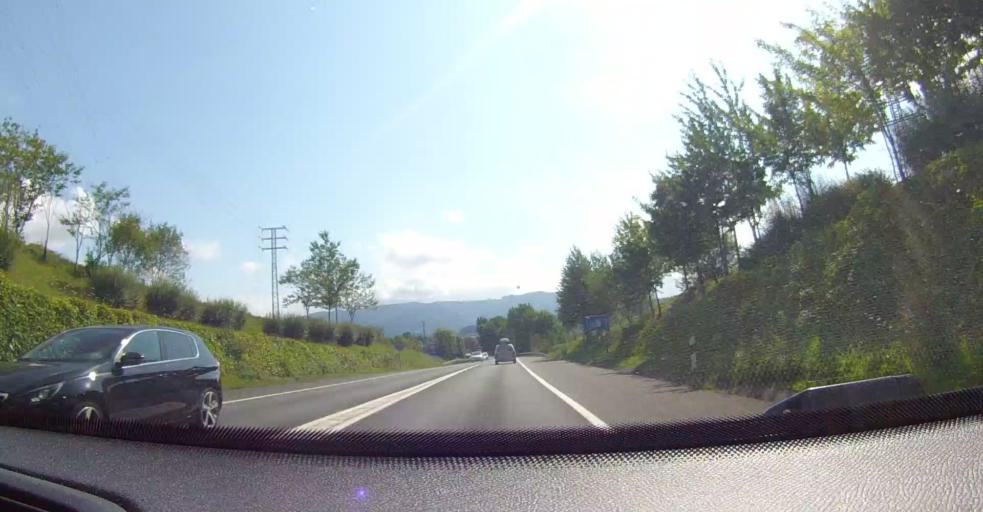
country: ES
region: Basque Country
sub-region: Bizkaia
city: Gernika-Lumo
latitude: 43.3165
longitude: -2.6690
